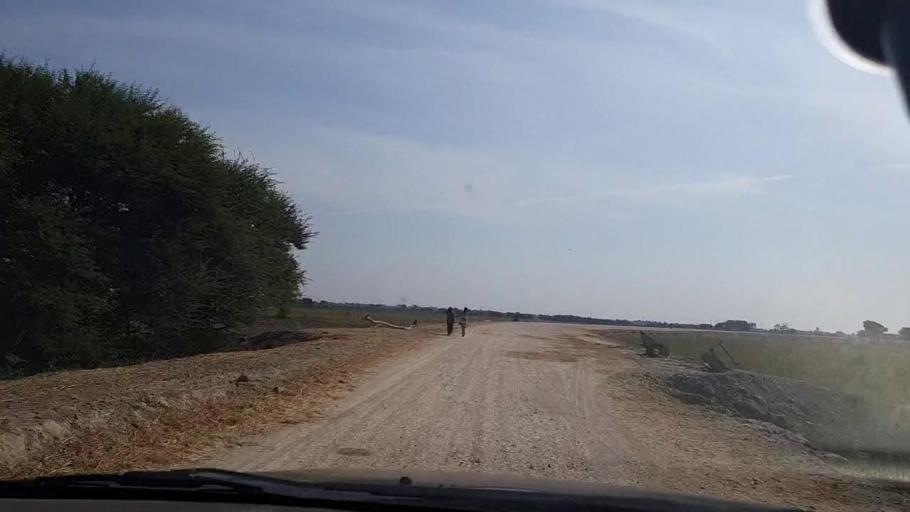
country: PK
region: Sindh
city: Mirpur Batoro
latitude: 24.7320
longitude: 68.2758
